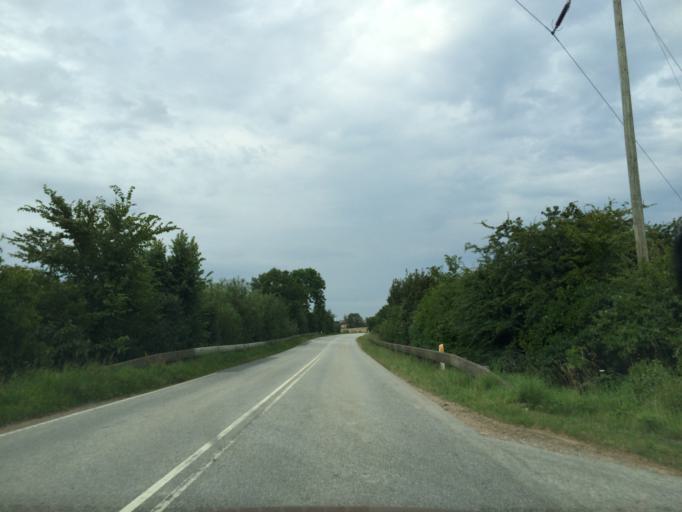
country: DK
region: South Denmark
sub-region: Sonderborg Kommune
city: Broager
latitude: 54.9070
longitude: 9.6762
